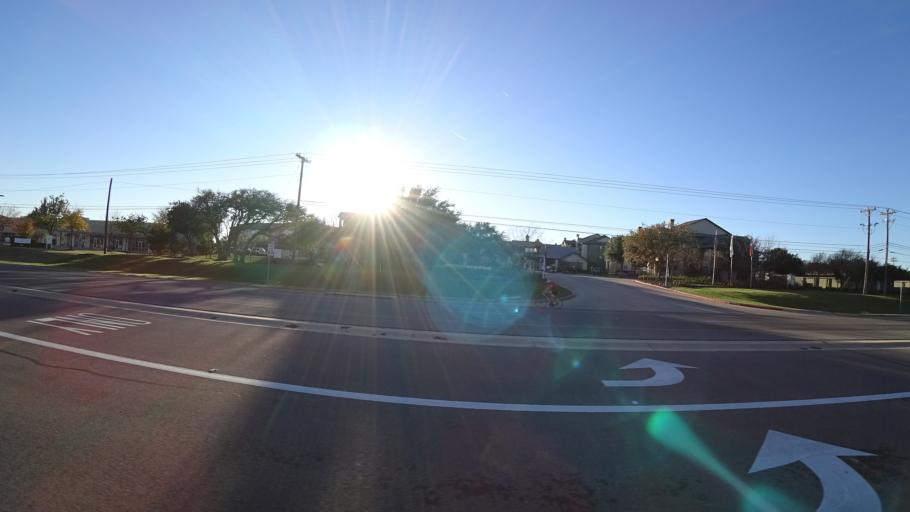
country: US
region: Texas
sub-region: Williamson County
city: Brushy Creek
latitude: 30.4896
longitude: -97.7719
